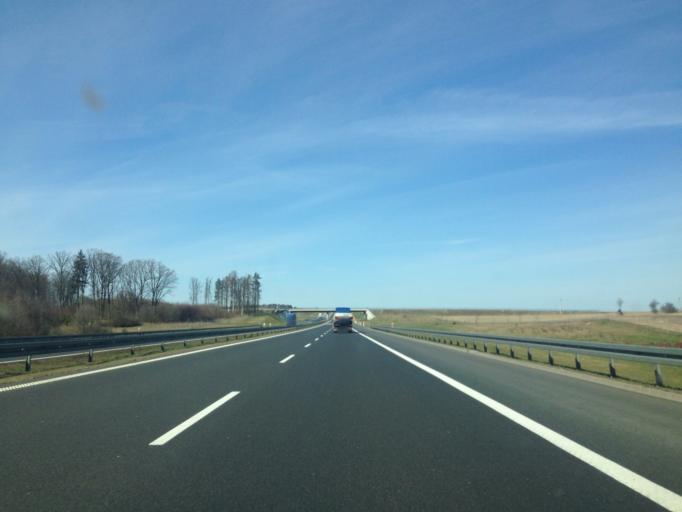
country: PL
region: Pomeranian Voivodeship
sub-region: Powiat starogardzki
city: Bobowo
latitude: 53.8346
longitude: 18.6284
